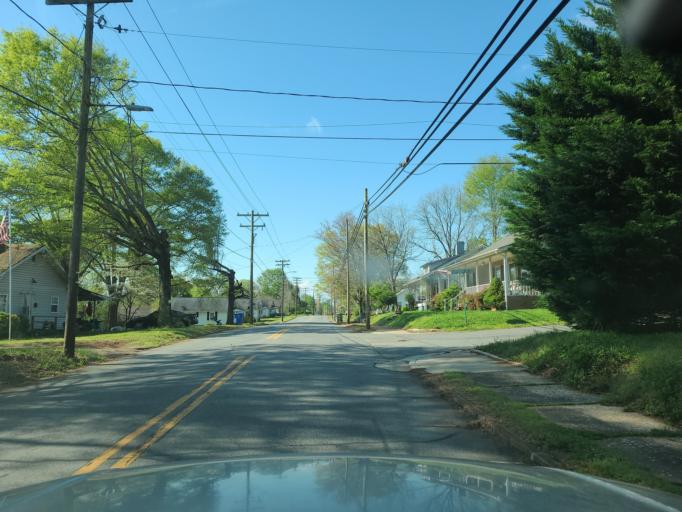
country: US
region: North Carolina
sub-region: Rutherford County
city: Spindale
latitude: 35.3691
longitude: -81.9268
